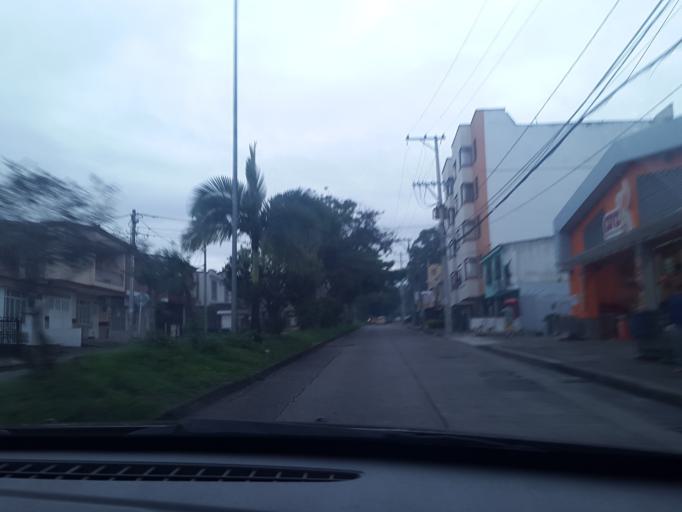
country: CO
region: Quindio
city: Armenia
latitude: 4.5427
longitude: -75.6847
